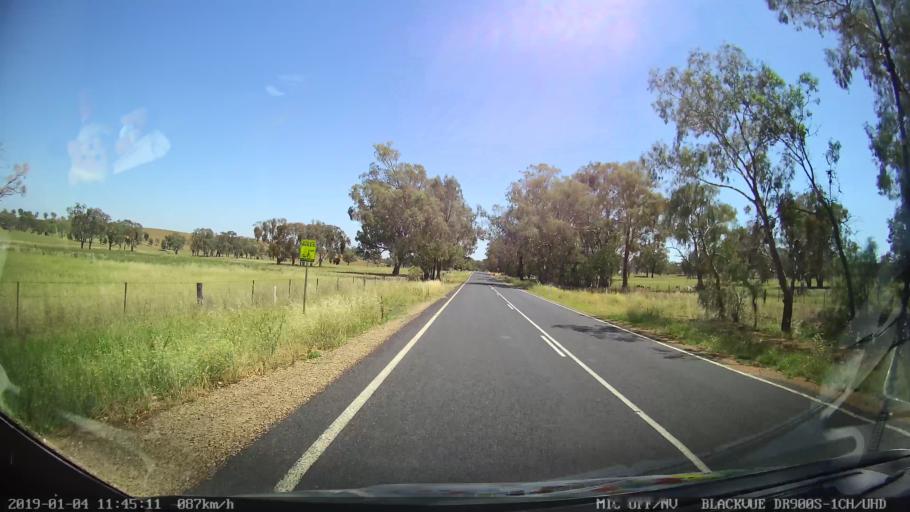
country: AU
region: New South Wales
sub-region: Cabonne
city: Molong
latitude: -32.9569
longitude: 148.7643
